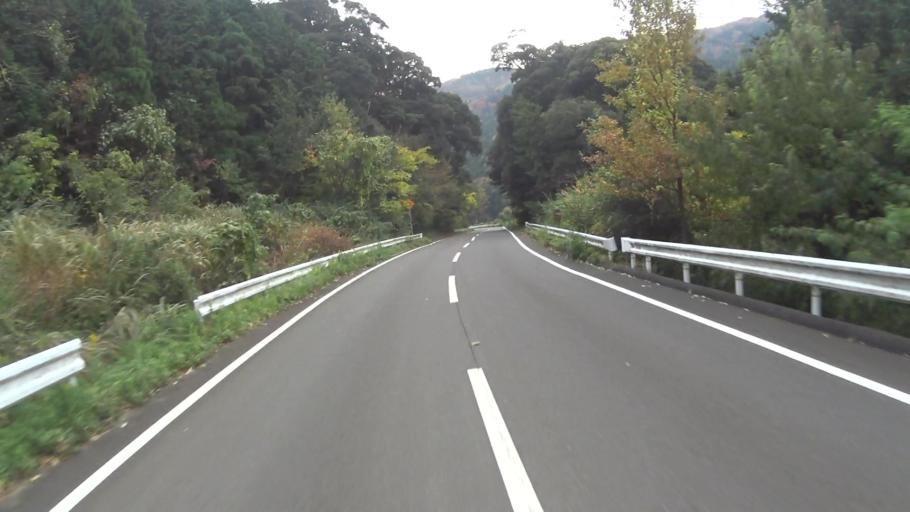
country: JP
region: Kyoto
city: Maizuru
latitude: 35.5637
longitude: 135.4568
